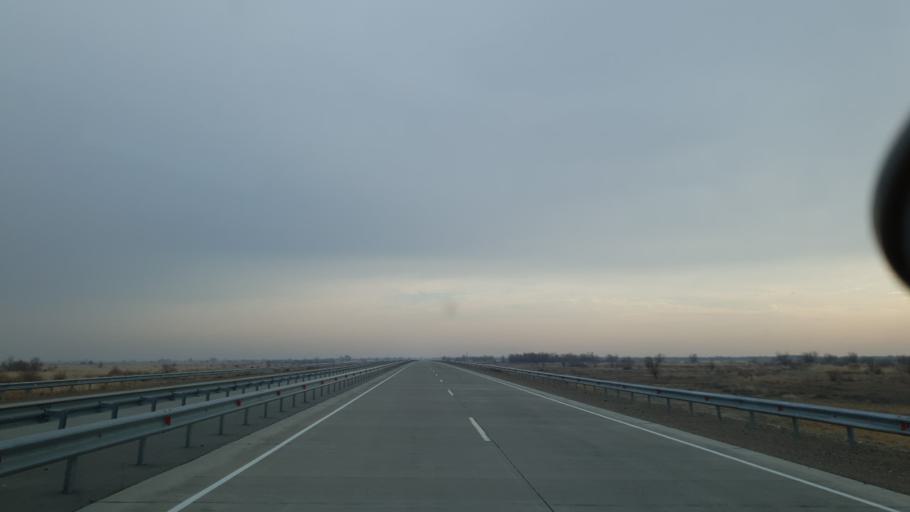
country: KZ
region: Almaty Oblysy
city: Zharkent
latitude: 44.0162
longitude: 79.7632
